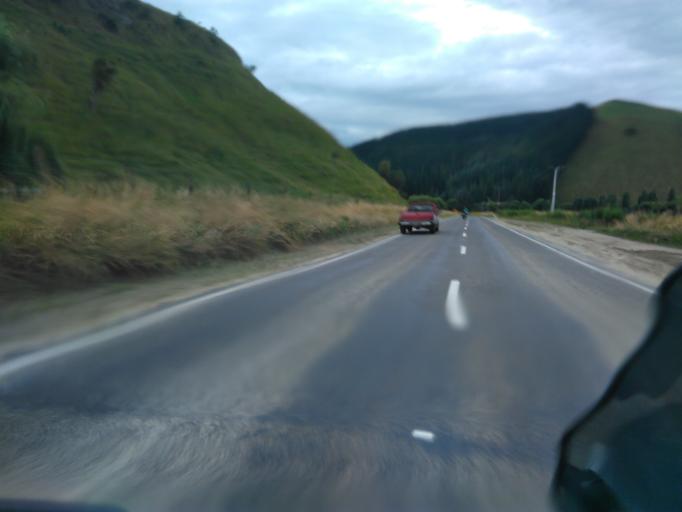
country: NZ
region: Gisborne
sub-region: Gisborne District
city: Gisborne
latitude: -38.4617
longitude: 177.7411
